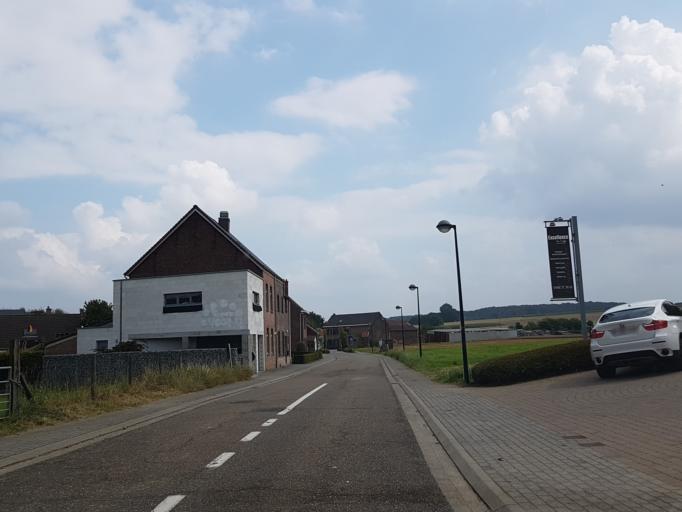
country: BE
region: Flanders
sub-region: Provincie Vlaams-Brabant
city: Kortenberg
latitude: 50.8769
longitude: 4.5527
